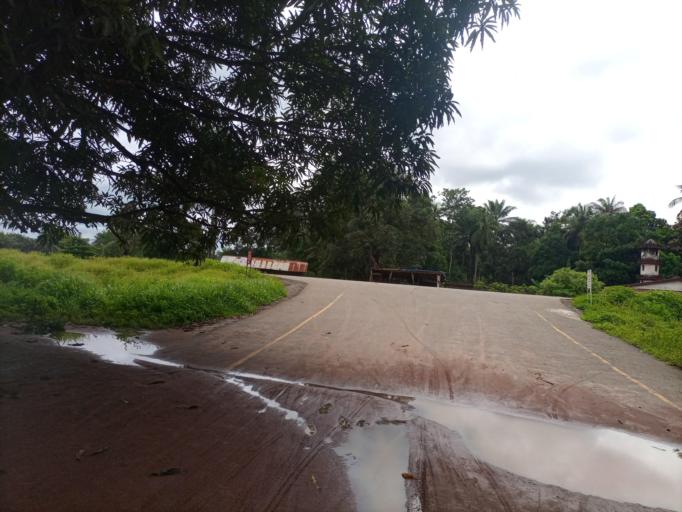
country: SL
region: Northern Province
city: Sawkta
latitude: 8.6384
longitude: -13.1894
